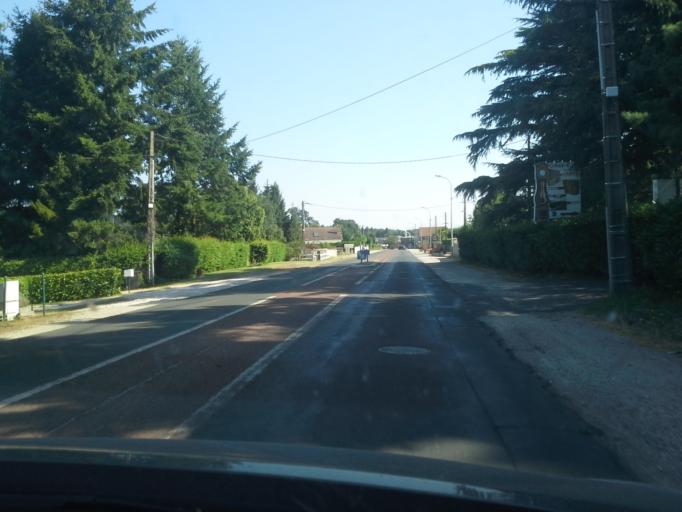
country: FR
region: Centre
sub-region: Departement du Loir-et-Cher
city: Les Montils
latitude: 47.5165
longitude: 1.2999
